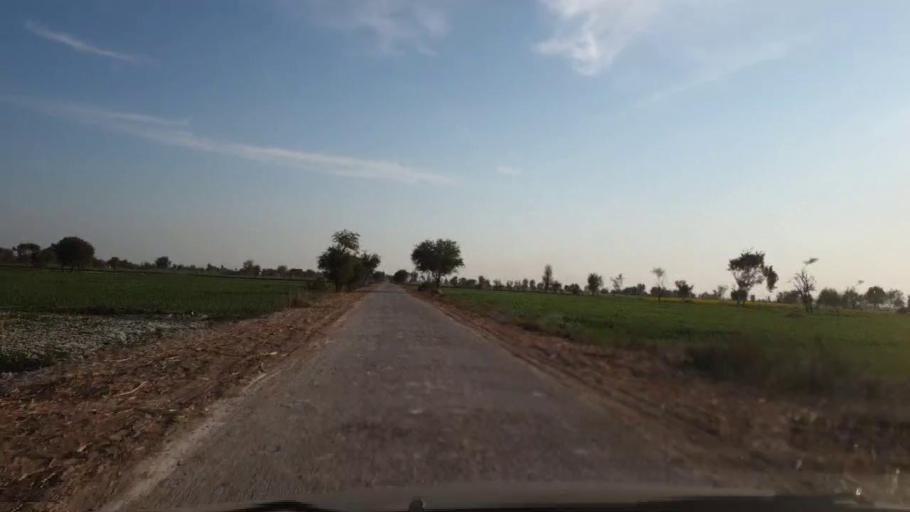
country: PK
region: Sindh
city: Khadro
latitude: 26.1986
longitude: 68.7468
